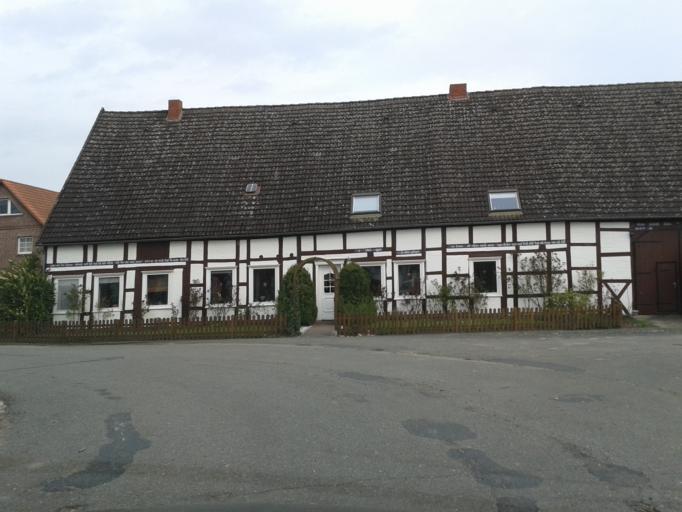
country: DE
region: Lower Saxony
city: Lubbow
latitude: 52.9056
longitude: 11.1802
